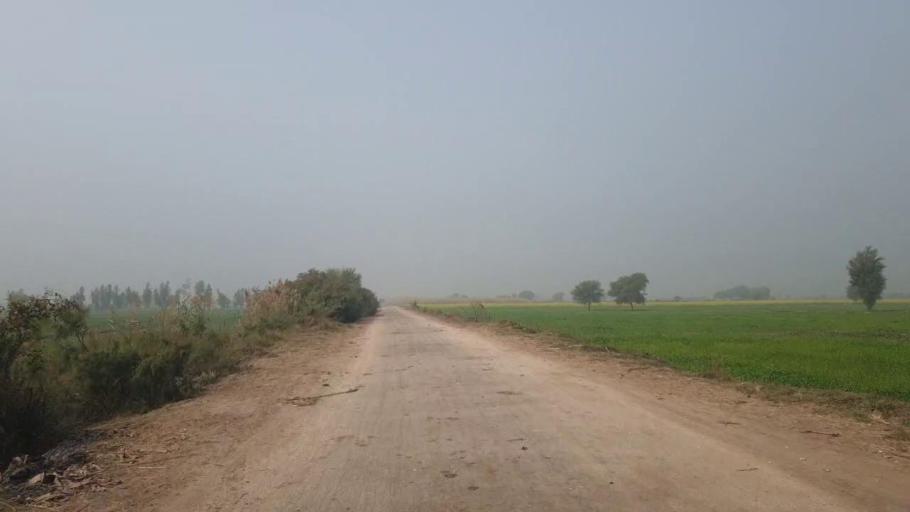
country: PK
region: Sindh
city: Bhit Shah
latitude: 25.8158
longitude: 68.5740
